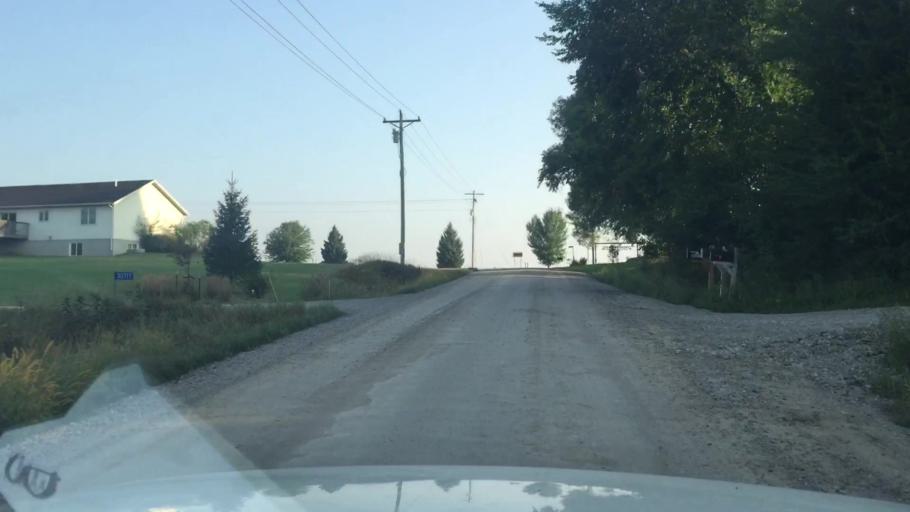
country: US
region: Iowa
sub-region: Story County
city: Huxley
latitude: 41.9106
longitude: -93.5746
